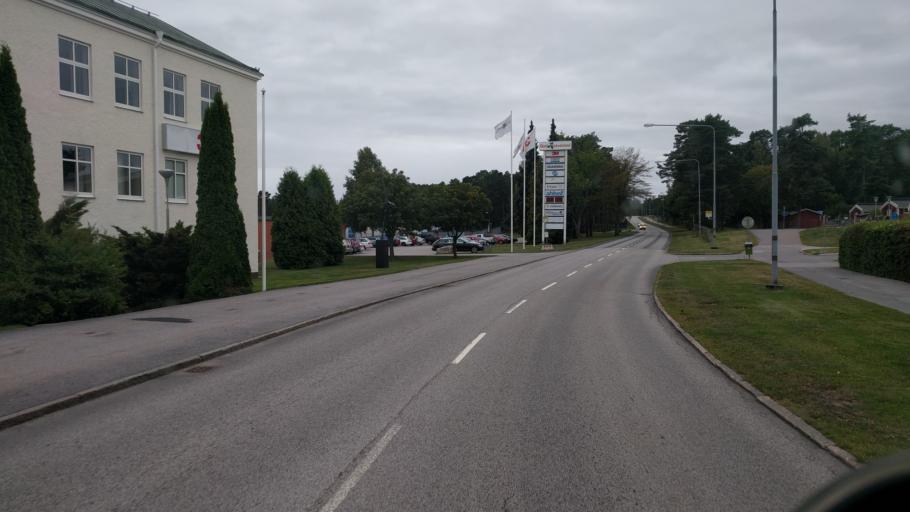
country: SE
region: Kalmar
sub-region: Vasterviks Kommun
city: Vaestervik
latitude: 57.7544
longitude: 16.6235
